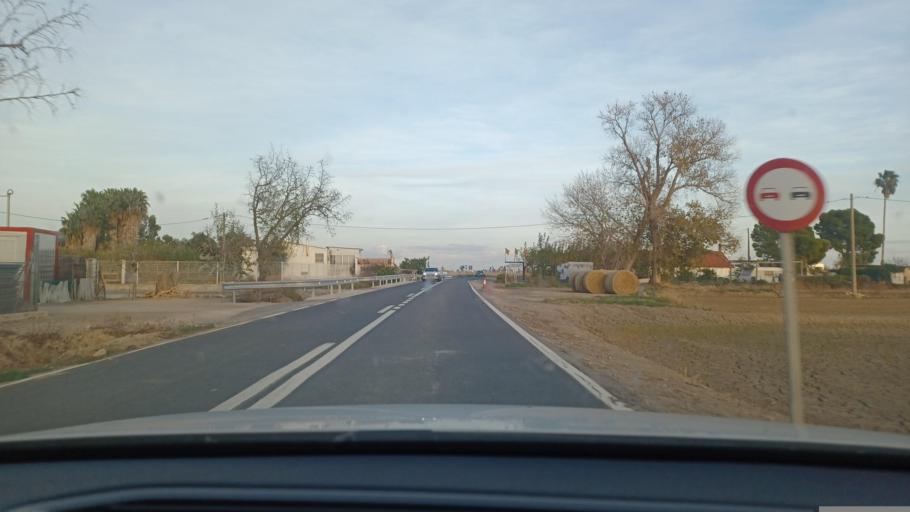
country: ES
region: Catalonia
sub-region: Provincia de Tarragona
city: Amposta
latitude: 40.7048
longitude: 0.6233
